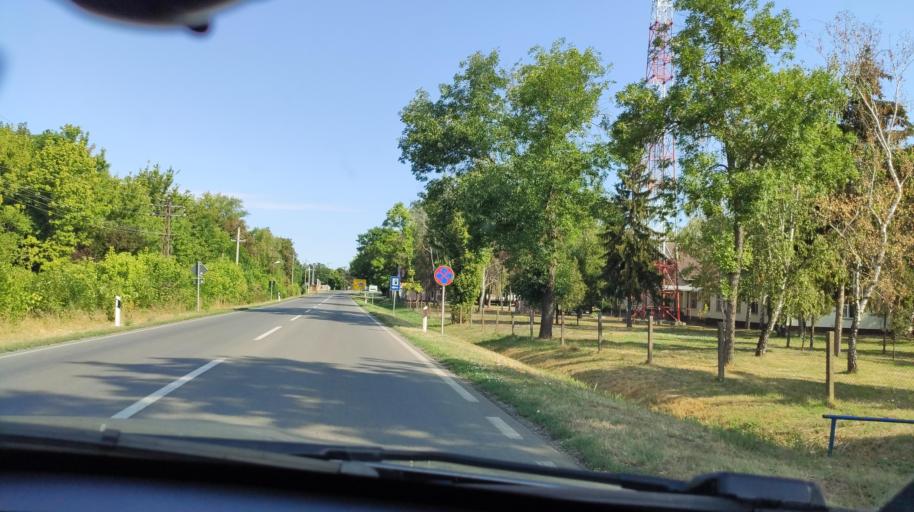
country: RS
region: Autonomna Pokrajina Vojvodina
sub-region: Severnobacki Okrug
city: Backa Topola
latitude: 45.8041
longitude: 19.6321
